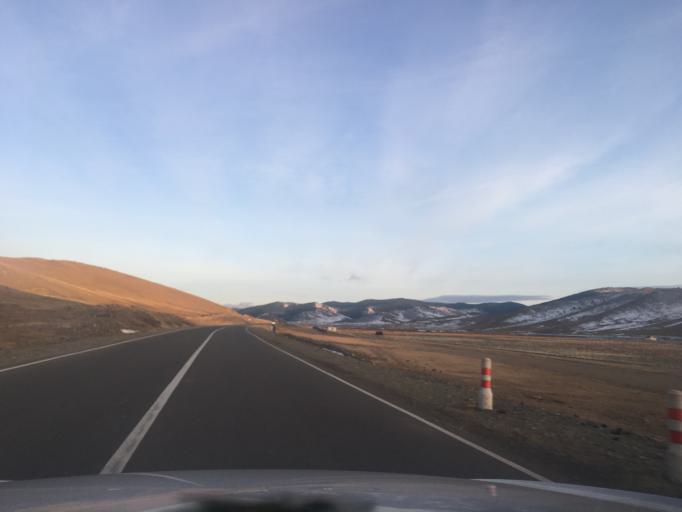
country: MN
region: Central Aimak
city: Mandal
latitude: 48.1140
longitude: 106.7022
